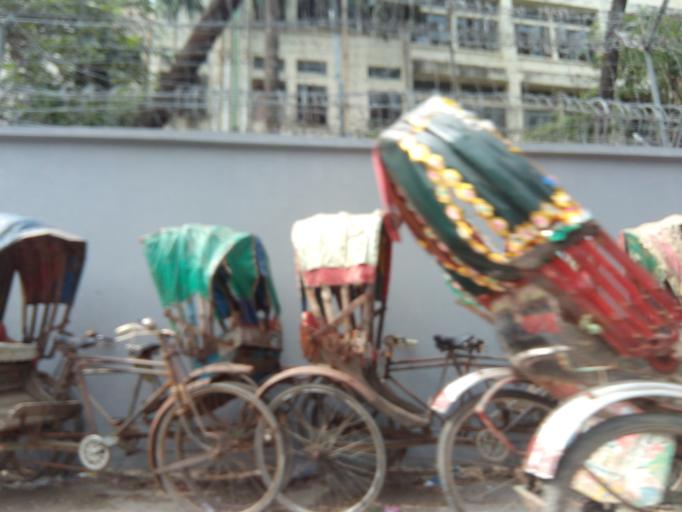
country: BD
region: Dhaka
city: Azimpur
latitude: 23.7319
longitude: 90.3711
